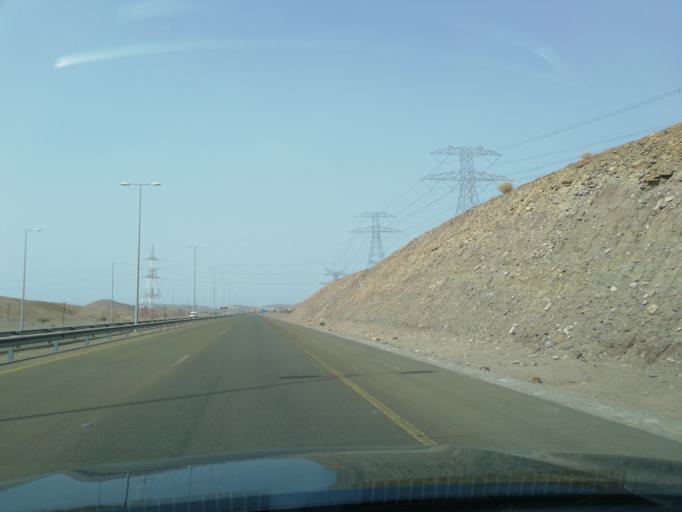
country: OM
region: Al Batinah
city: Al Liwa'
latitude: 24.3536
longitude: 56.5236
